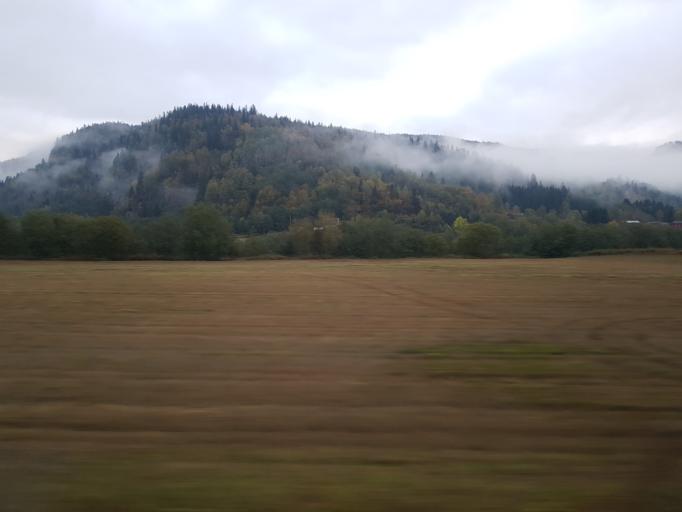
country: NO
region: Sor-Trondelag
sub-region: Midtre Gauldal
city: Storen
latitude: 63.0946
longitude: 10.2391
